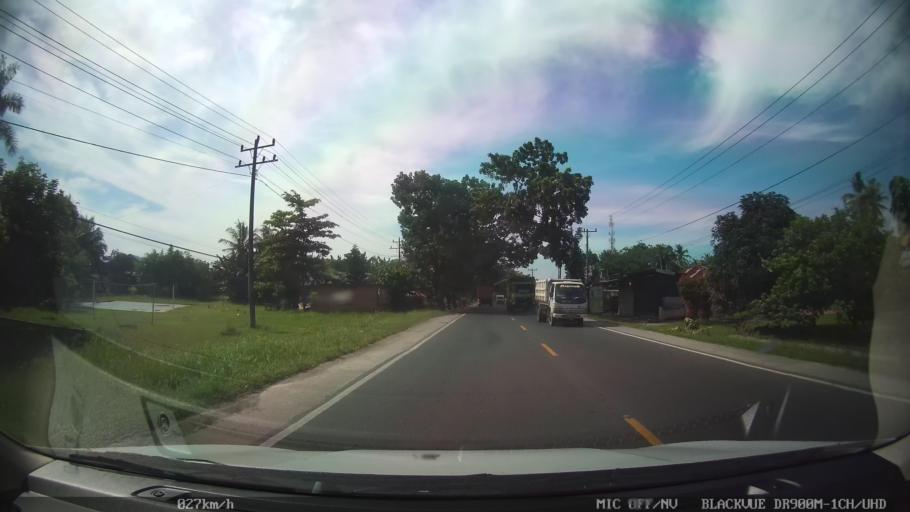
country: ID
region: North Sumatra
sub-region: Kabupaten Langkat
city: Stabat
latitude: 3.7169
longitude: 98.5037
